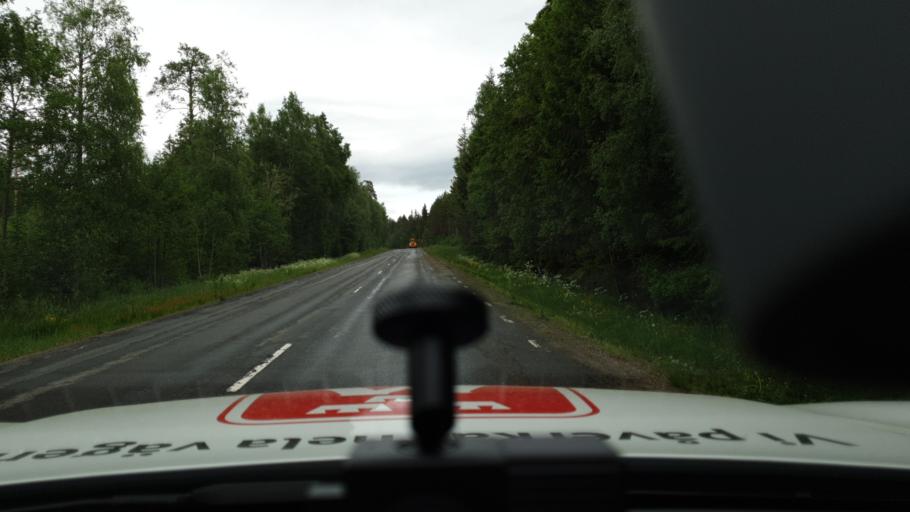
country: SE
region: Joenkoeping
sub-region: Mullsjo Kommun
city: Mullsjoe
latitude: 57.9841
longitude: 13.8022
